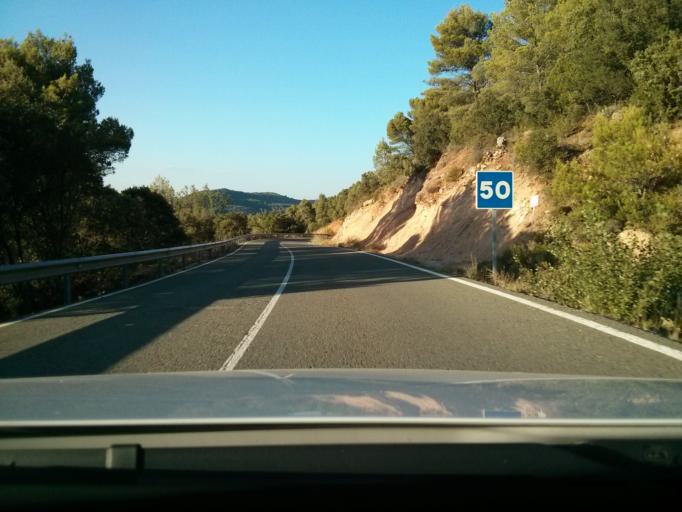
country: ES
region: Castille-La Mancha
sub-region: Provincia de Guadalajara
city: Chillaron del Rey
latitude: 40.6086
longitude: -2.6928
